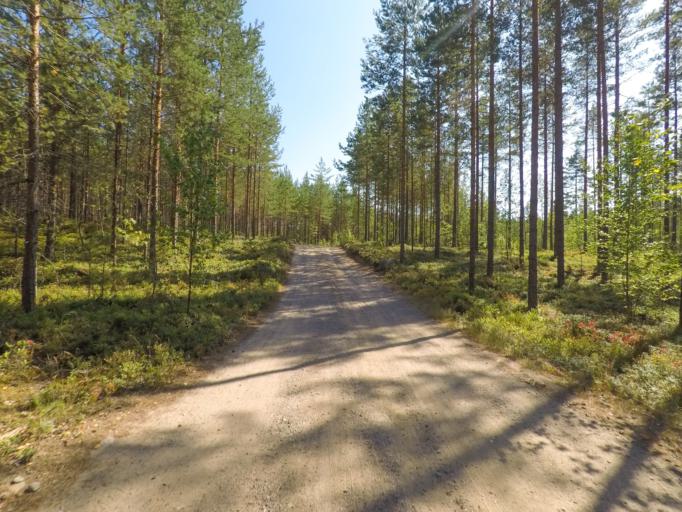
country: FI
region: Southern Savonia
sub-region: Mikkeli
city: Puumala
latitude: 61.4277
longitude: 28.0075
